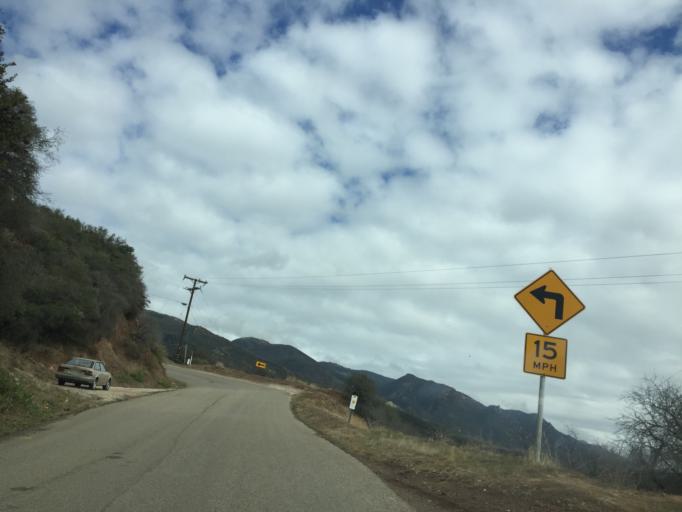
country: US
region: California
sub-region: Santa Barbara County
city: Goleta
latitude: 34.4779
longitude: -119.7960
